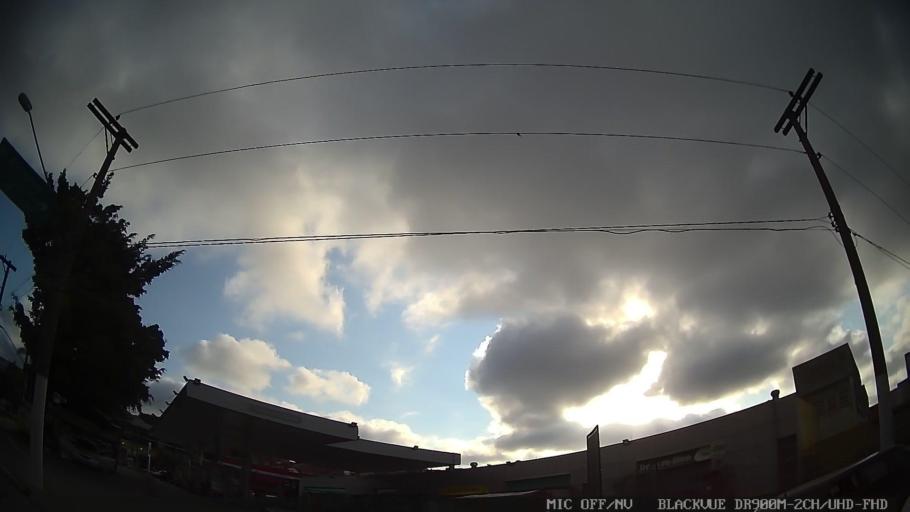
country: BR
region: Sao Paulo
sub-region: Sao Caetano Do Sul
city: Sao Caetano do Sul
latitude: -23.5522
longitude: -46.4928
